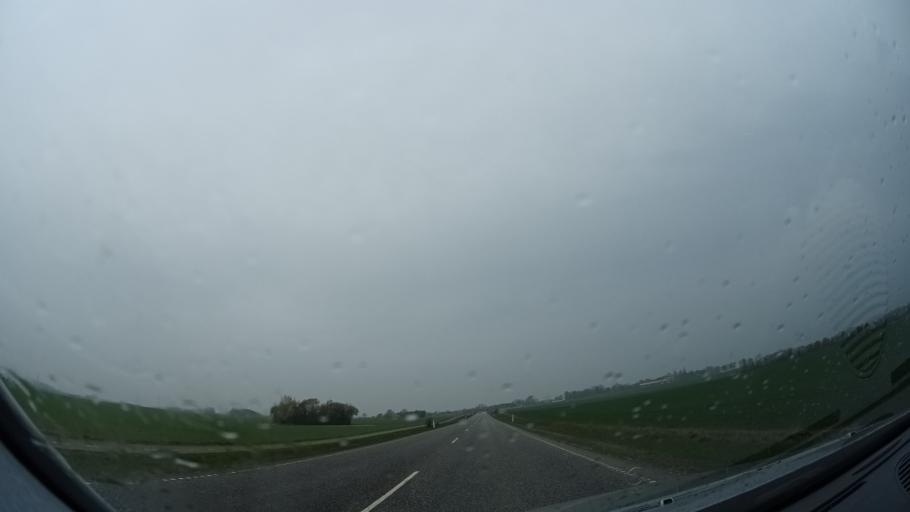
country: DK
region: Zealand
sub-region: Holbaek Kommune
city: Holbaek
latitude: 55.7372
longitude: 11.6281
